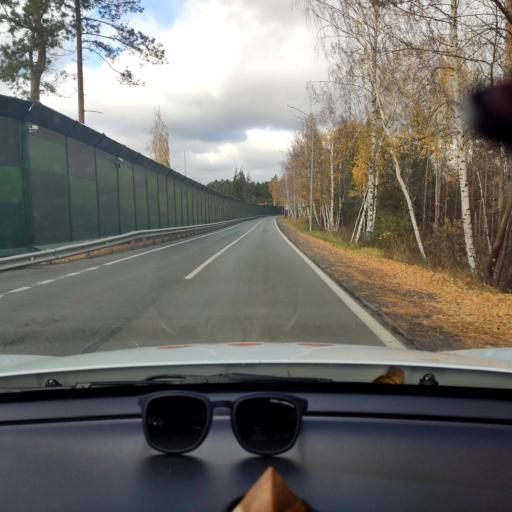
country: RU
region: Tatarstan
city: Verkhniy Uslon
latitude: 55.6264
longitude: 49.0139
